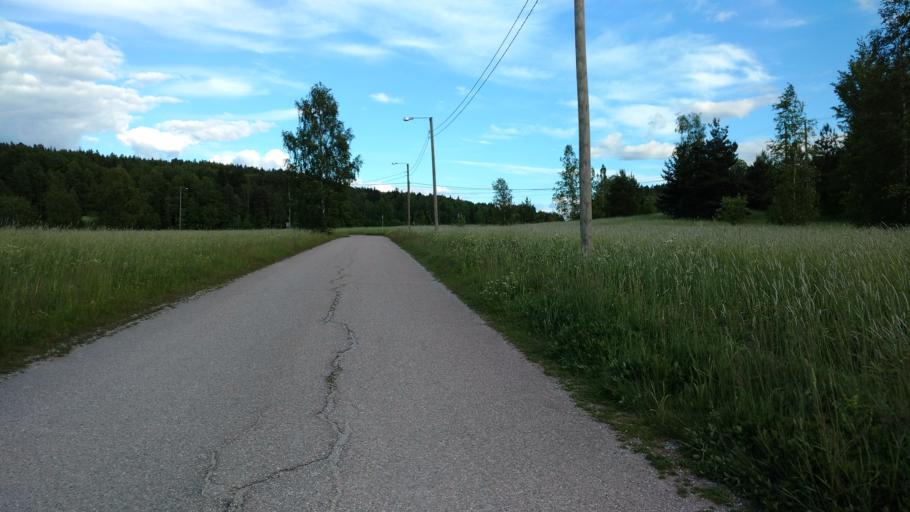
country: FI
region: Varsinais-Suomi
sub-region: Salo
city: Salo
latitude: 60.3874
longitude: 23.1661
